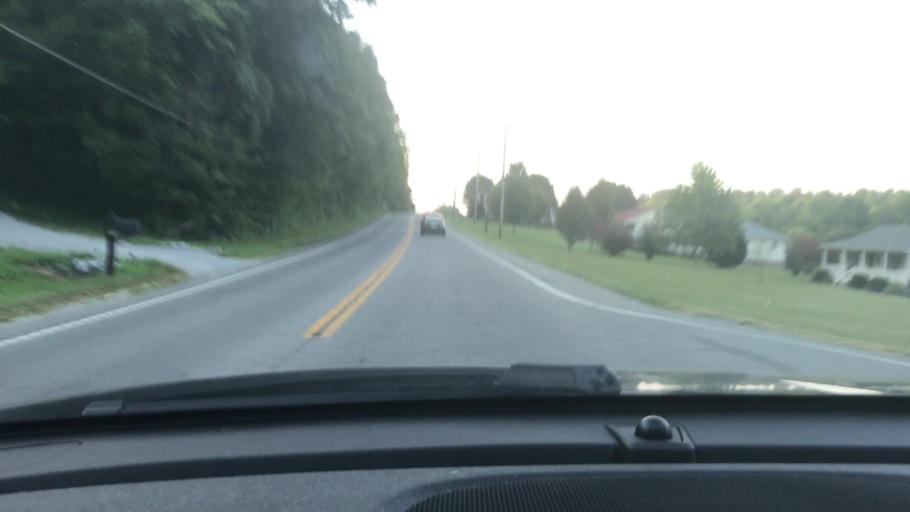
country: US
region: Tennessee
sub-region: Dickson County
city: Dickson
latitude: 36.1224
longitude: -87.3608
